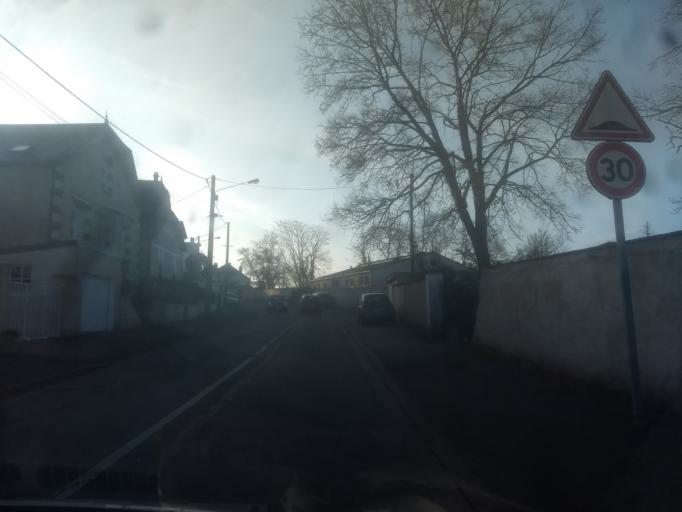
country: FR
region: Centre
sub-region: Departement du Cher
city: Bourges
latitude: 47.1010
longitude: 2.3937
